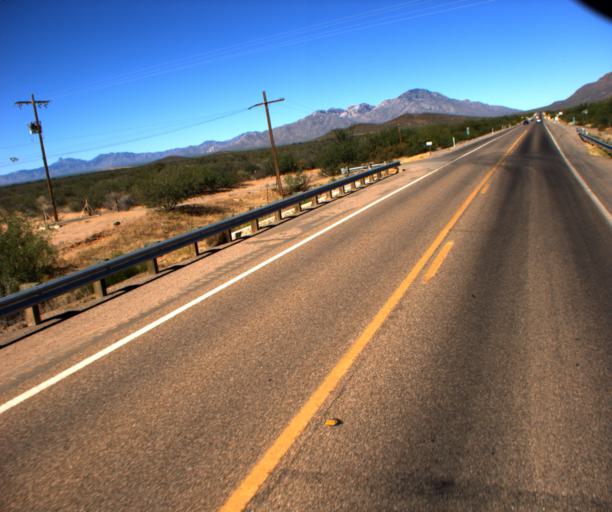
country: US
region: Arizona
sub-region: Pima County
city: Three Points
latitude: 32.0662
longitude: -111.3679
